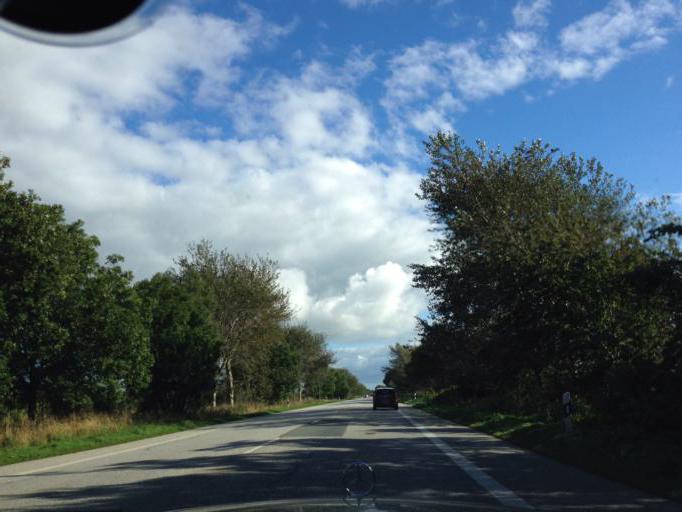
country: DE
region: Schleswig-Holstein
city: Risum-Lindholm
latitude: 54.7587
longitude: 8.8827
